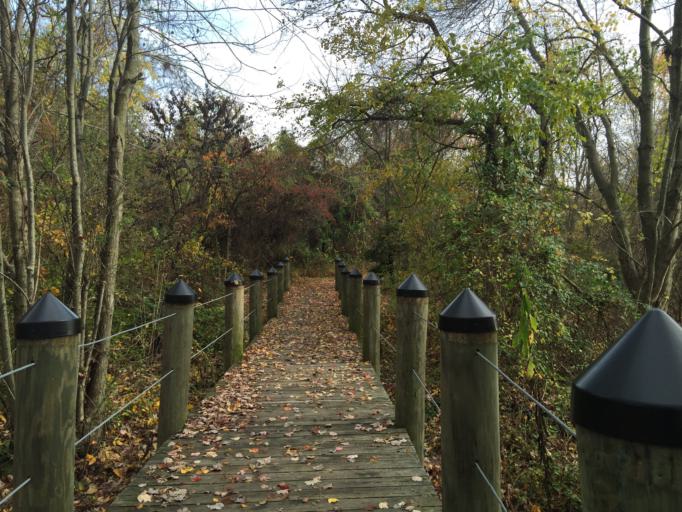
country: US
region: Maryland
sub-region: Carroll County
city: Sykesville
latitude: 39.2762
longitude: -77.0199
